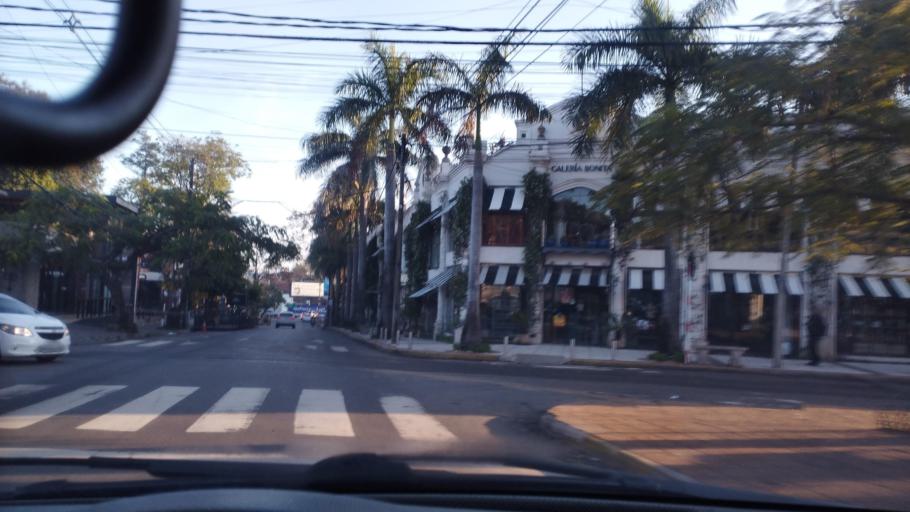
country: PY
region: Asuncion
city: Asuncion
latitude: -25.2869
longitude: -57.5768
